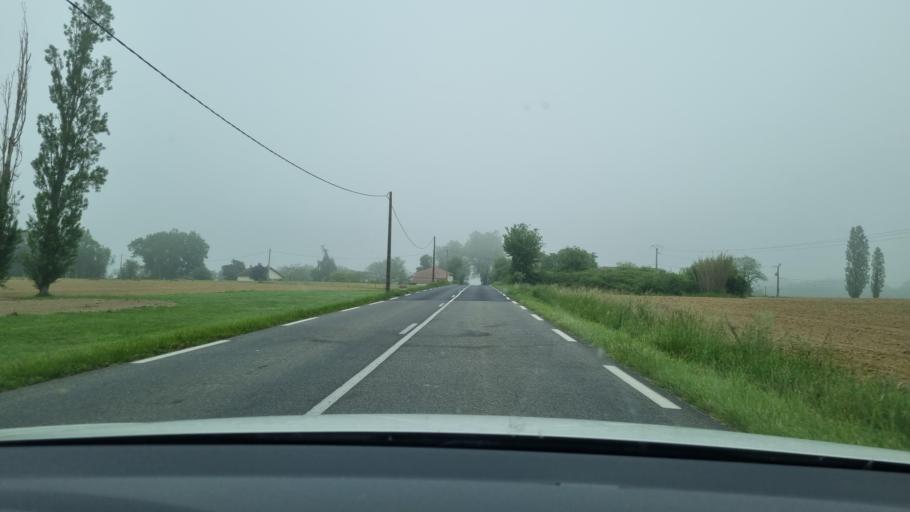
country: FR
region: Aquitaine
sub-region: Departement des Landes
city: Amou
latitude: 43.5364
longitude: -0.6897
